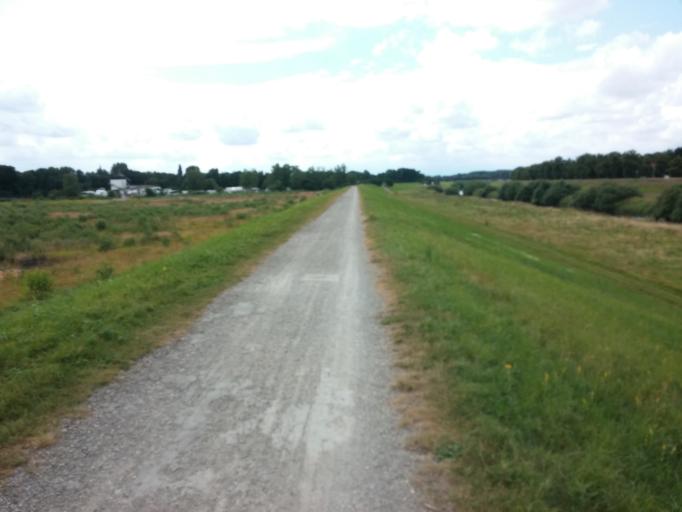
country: DE
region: North Rhine-Westphalia
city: Dorsten
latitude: 51.6650
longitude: 6.9834
